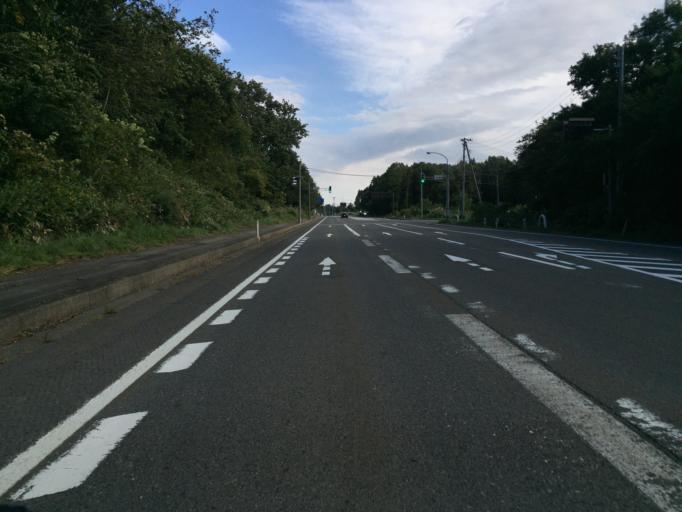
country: JP
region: Fukushima
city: Inawashiro
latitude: 37.5204
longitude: 139.9878
